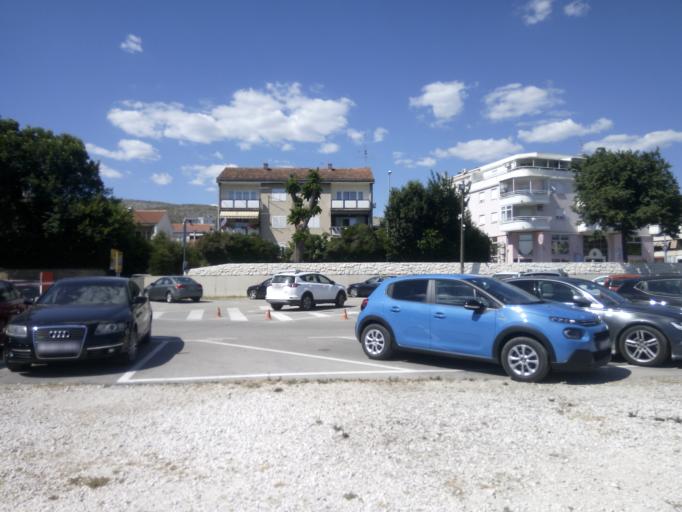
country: HR
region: Splitsko-Dalmatinska
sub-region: Grad Trogir
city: Trogir
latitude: 43.5181
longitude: 16.2525
